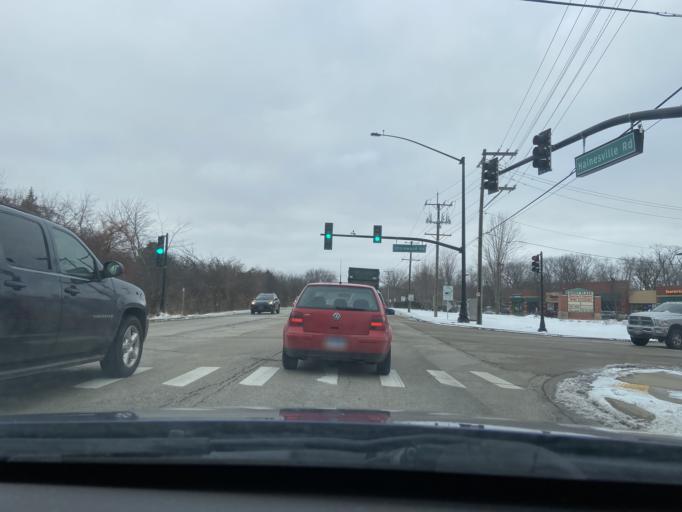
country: US
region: Illinois
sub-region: Lake County
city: Round Lake Park
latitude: 42.3718
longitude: -88.0666
